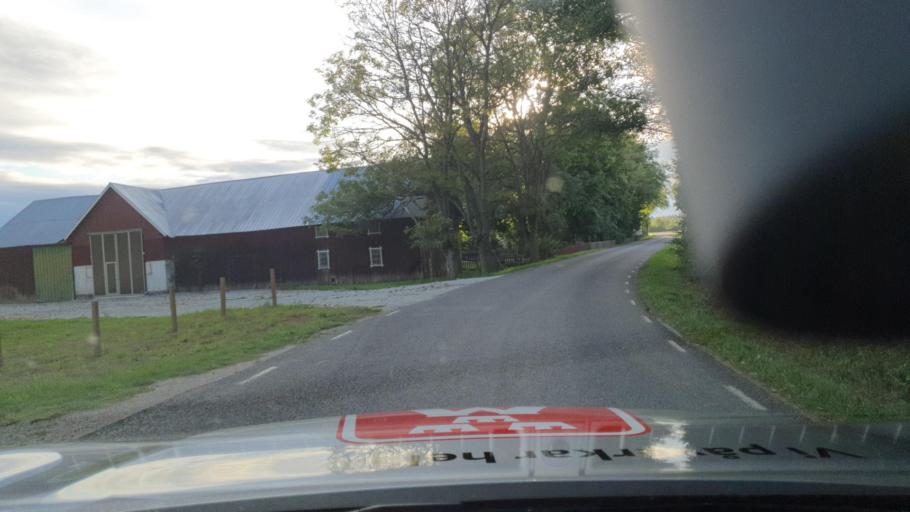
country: SE
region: Gotland
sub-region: Gotland
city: Vibble
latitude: 57.4946
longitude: 18.3263
